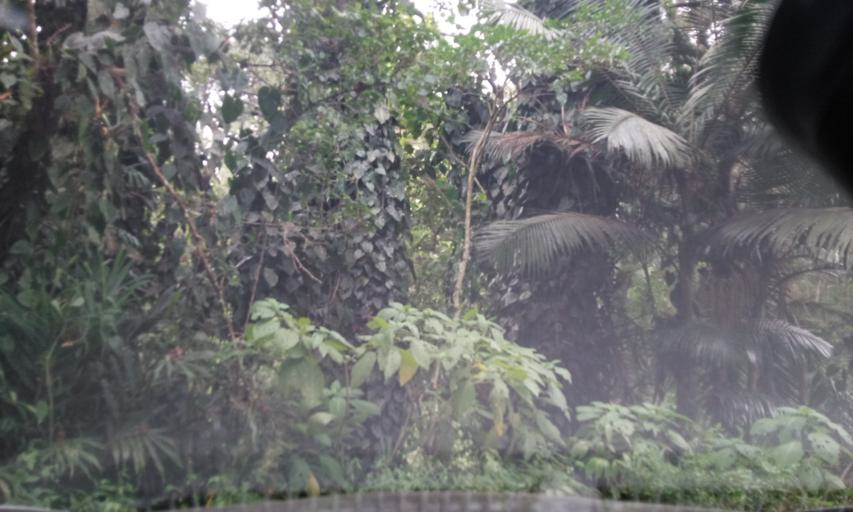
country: BR
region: Sao Paulo
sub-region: Sao Bernardo Do Campo
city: Sao Bernardo do Campo
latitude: -23.7943
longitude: -46.5339
